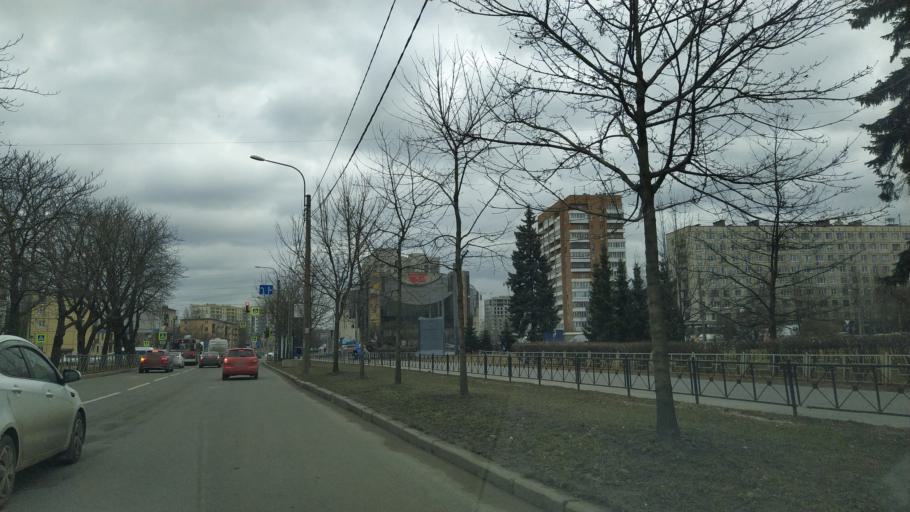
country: RU
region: St.-Petersburg
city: Centralniy
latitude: 59.9292
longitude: 30.4187
